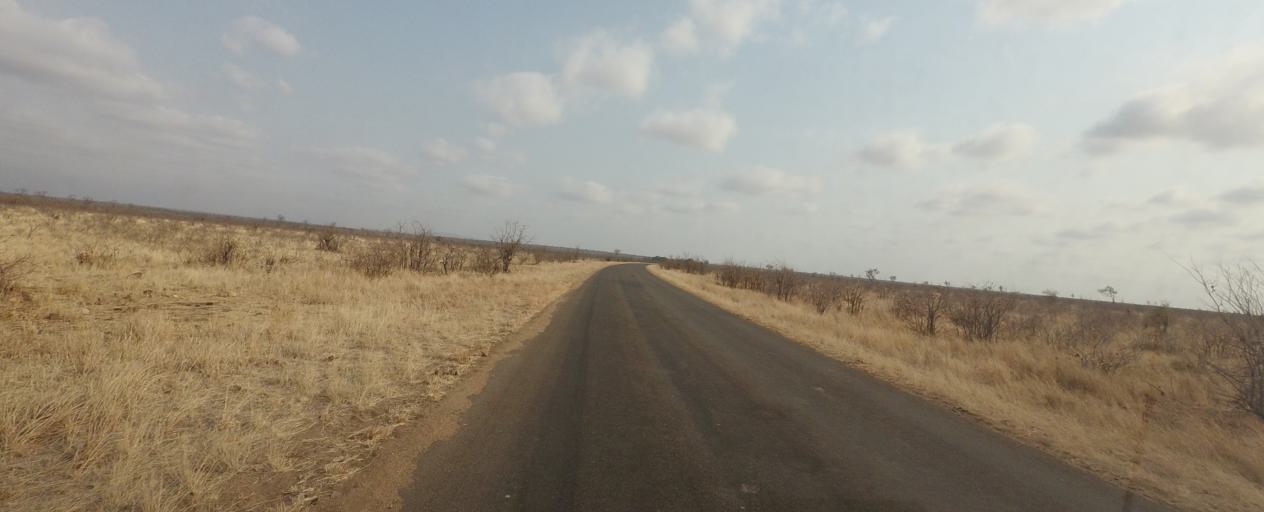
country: ZA
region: Limpopo
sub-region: Vhembe District Municipality
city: Mutale
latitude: -22.9161
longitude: 31.2535
